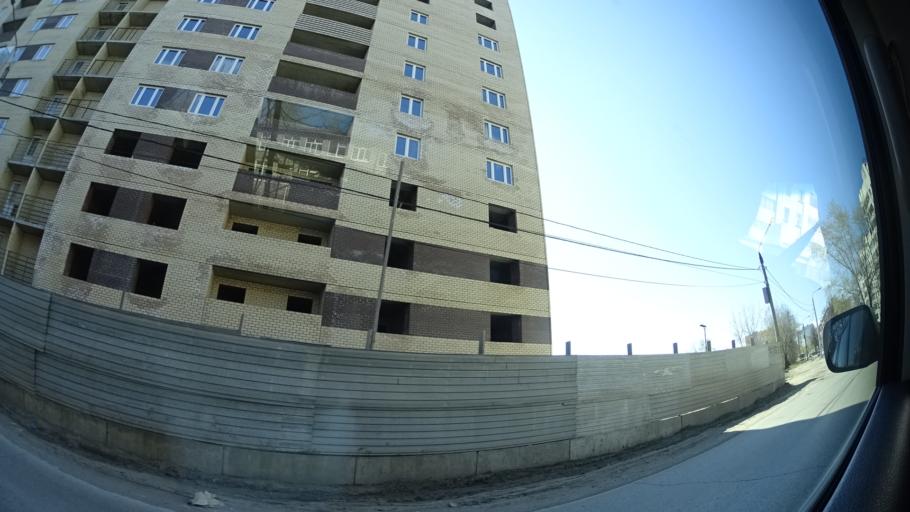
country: RU
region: Perm
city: Perm
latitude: 58.1096
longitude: 56.3115
